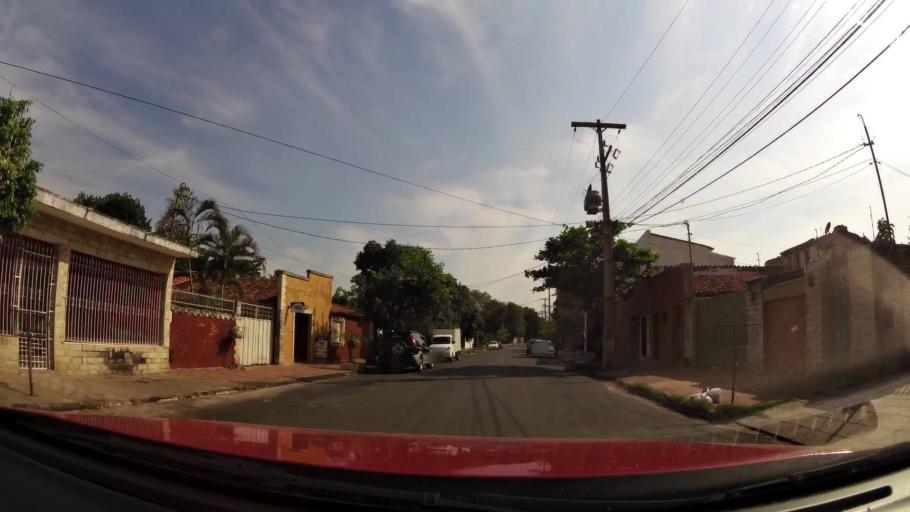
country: PY
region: Central
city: Fernando de la Mora
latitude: -25.2602
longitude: -57.5560
